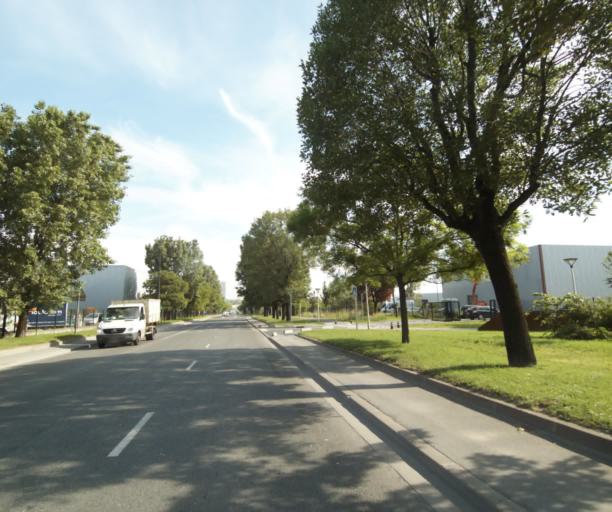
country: FR
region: Ile-de-France
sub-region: Departement des Hauts-de-Seine
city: Gennevilliers
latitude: 48.9433
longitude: 2.2951
